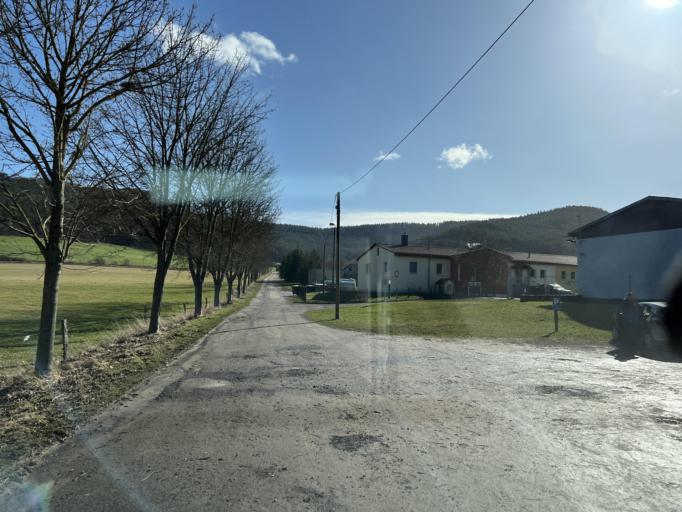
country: DE
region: Thuringia
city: Plaue
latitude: 50.7924
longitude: 10.9150
